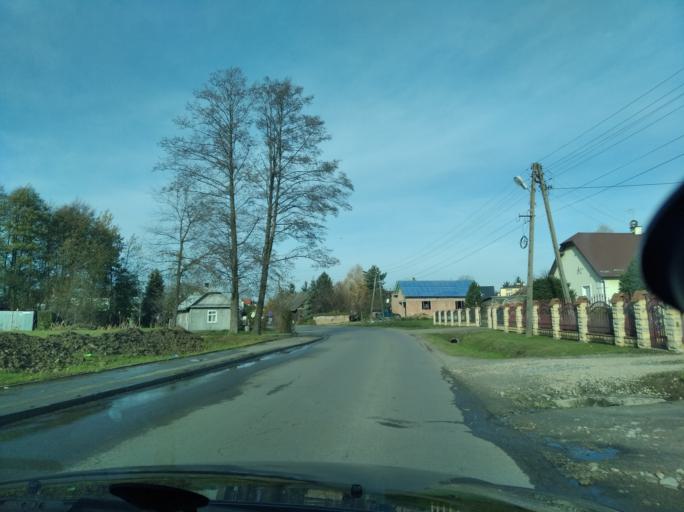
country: PL
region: Subcarpathian Voivodeship
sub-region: Powiat rzeszowski
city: Krasne
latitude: 50.0316
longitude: 22.0984
